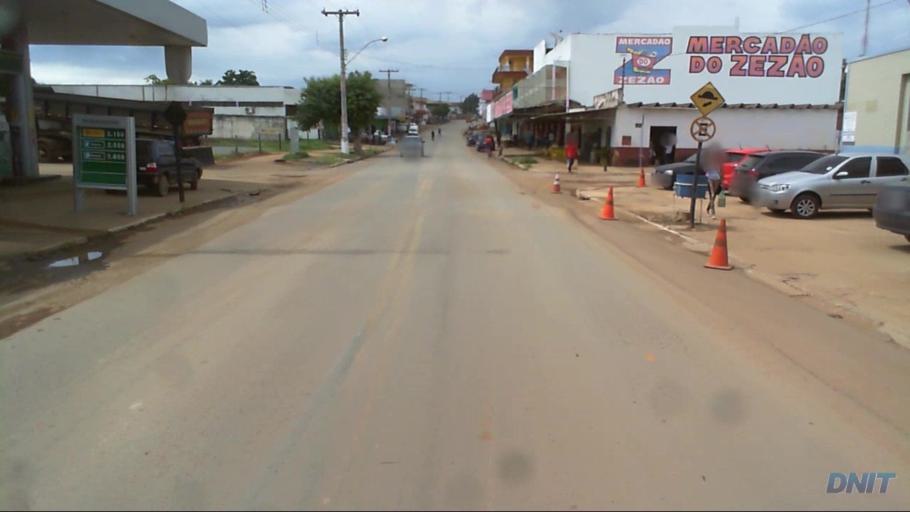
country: BR
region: Goias
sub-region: Padre Bernardo
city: Padre Bernardo
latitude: -15.1695
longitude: -48.2849
